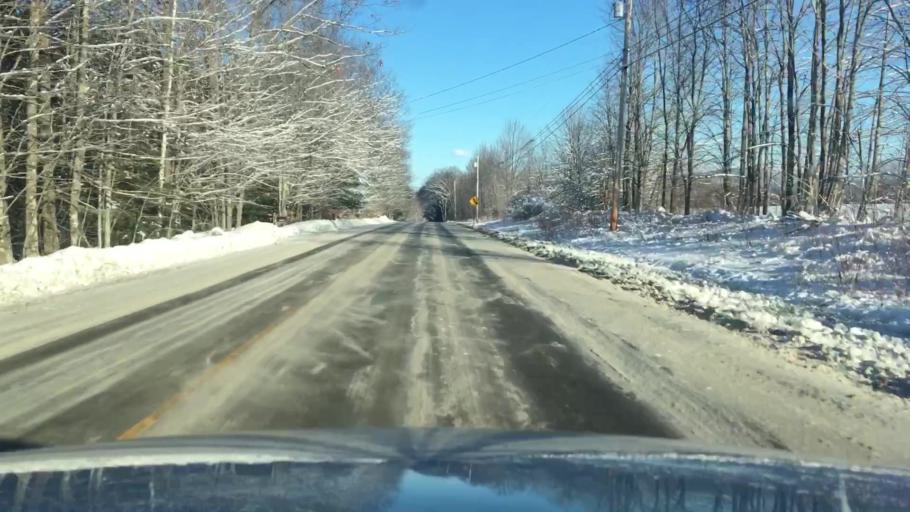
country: US
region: Maine
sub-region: Kennebec County
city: Mount Vernon
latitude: 44.4642
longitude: -69.9732
